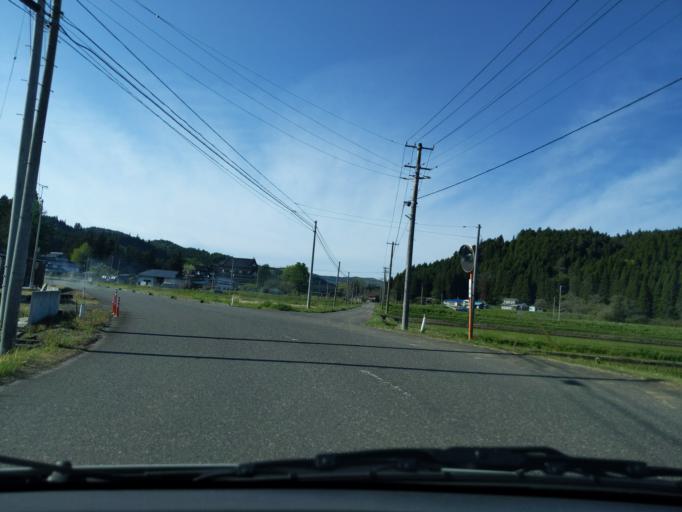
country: JP
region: Iwate
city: Ichinoseki
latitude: 38.8404
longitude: 140.9090
